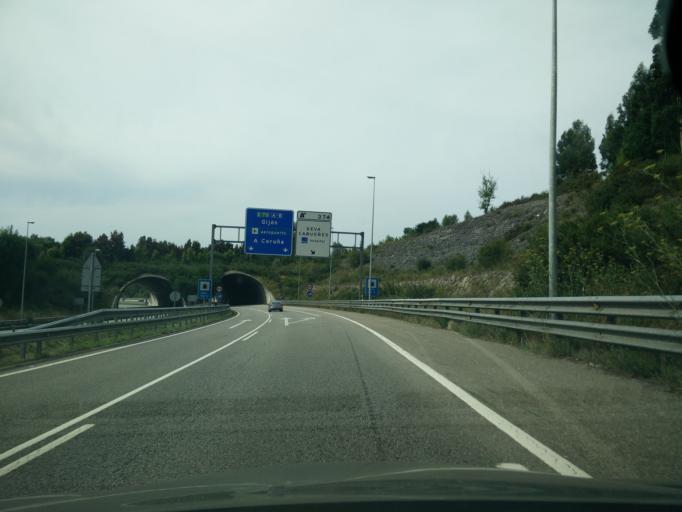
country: ES
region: Asturias
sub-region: Province of Asturias
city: Arriba
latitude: 43.5087
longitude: -5.5957
